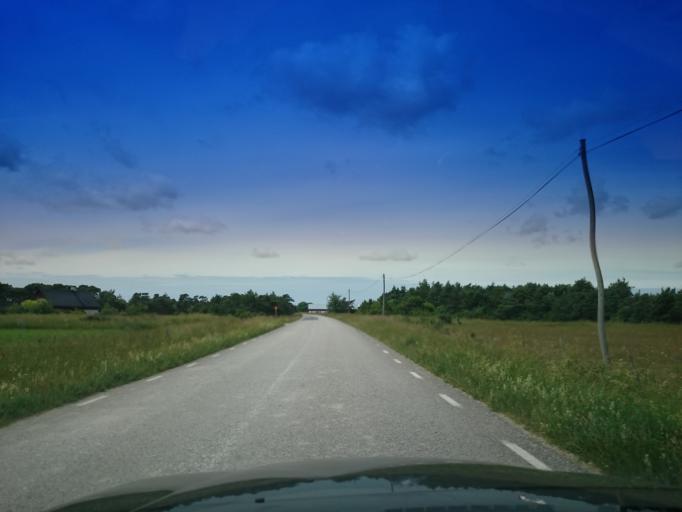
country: SE
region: Gotland
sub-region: Gotland
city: Hemse
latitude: 57.2545
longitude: 18.6015
